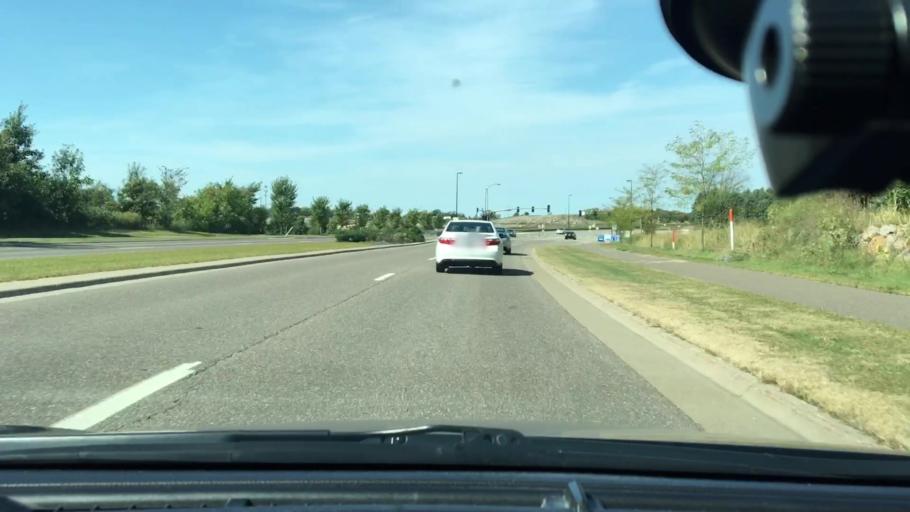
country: US
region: Minnesota
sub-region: Hennepin County
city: Corcoran
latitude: 45.0826
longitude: -93.5109
